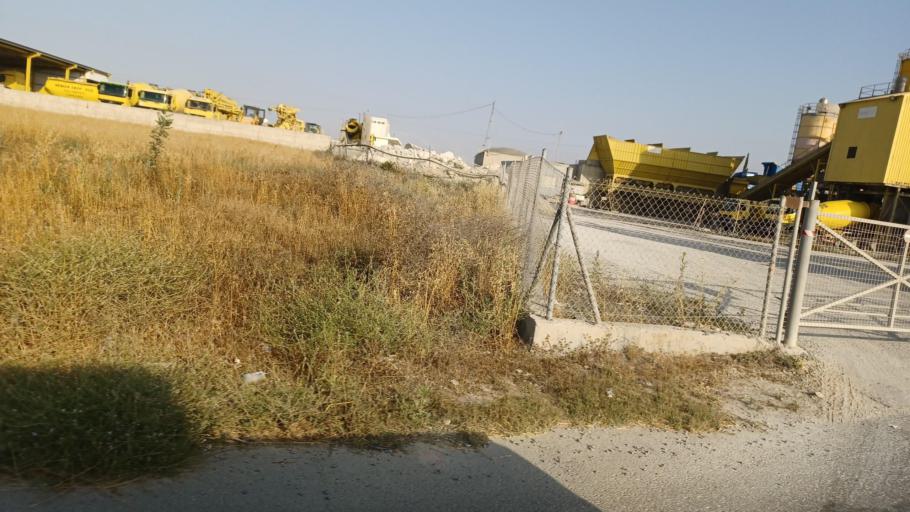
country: CY
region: Ammochostos
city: Paralimni
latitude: 35.0282
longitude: 33.9783
